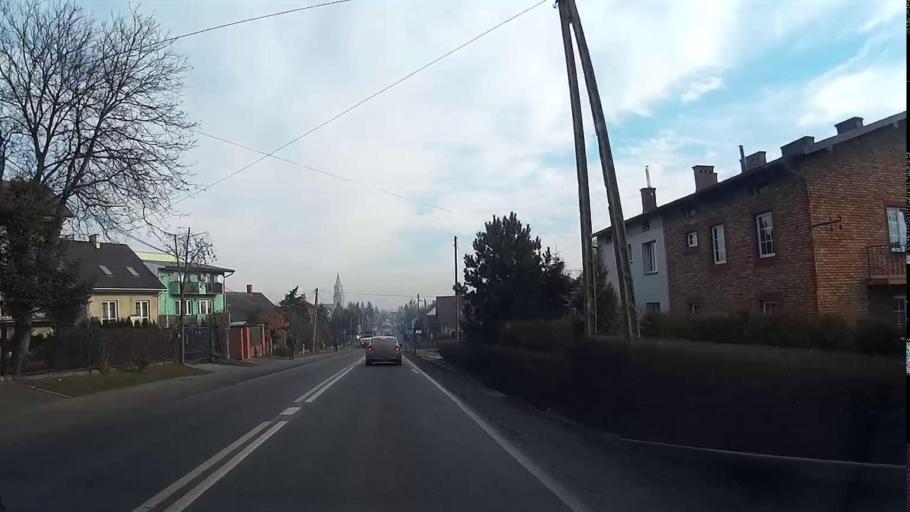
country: PL
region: Lesser Poland Voivodeship
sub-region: Powiat krakowski
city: Liszki
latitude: 50.0364
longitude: 19.7615
